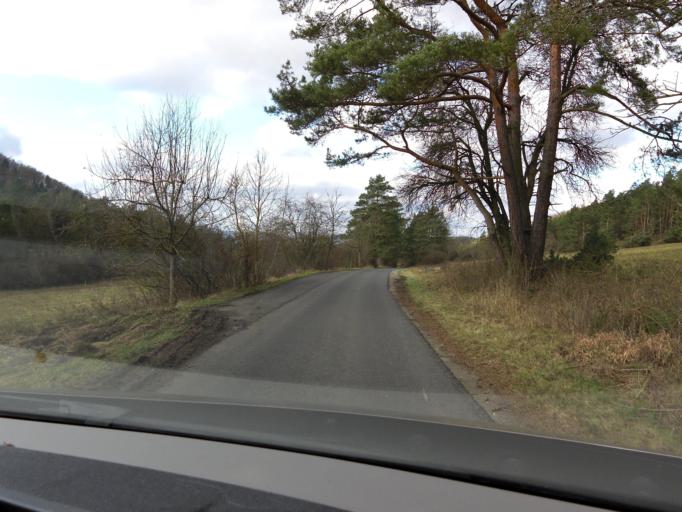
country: DE
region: Thuringia
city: Krauthausen
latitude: 51.0363
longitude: 10.2814
